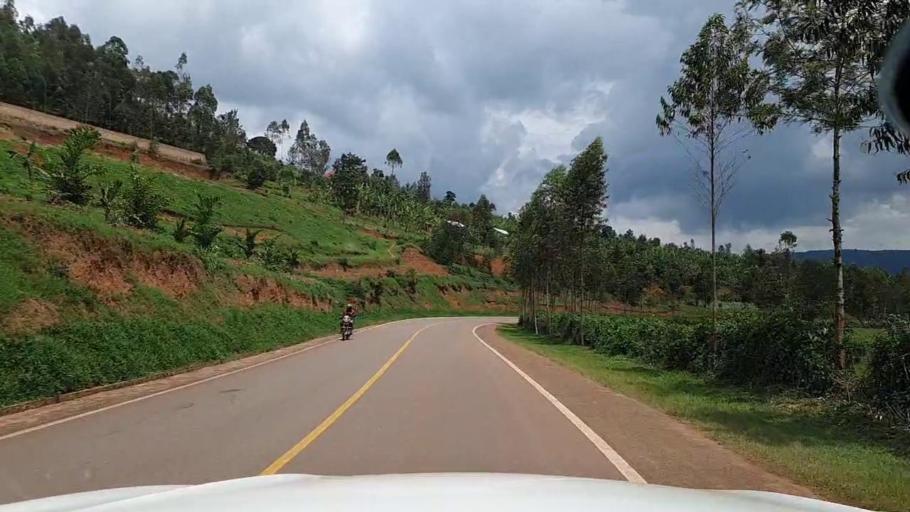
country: RW
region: Kigali
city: Kigali
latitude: -1.8057
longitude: 30.1260
